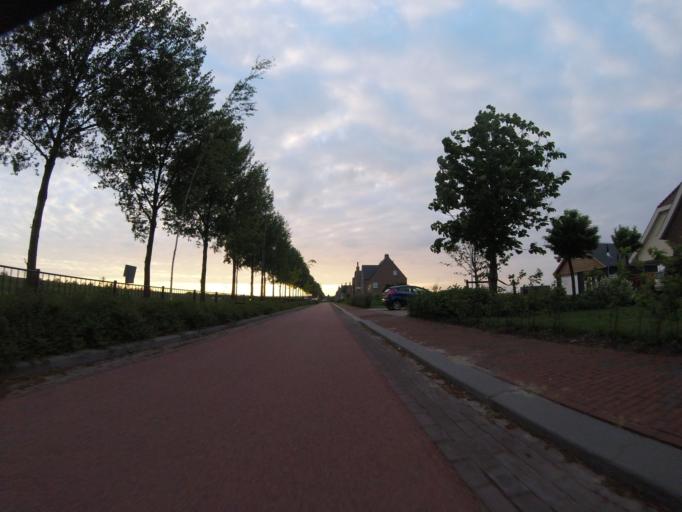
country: NL
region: North Holland
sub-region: Gemeente Haarlemmermeer
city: Hoofddorp
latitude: 52.2892
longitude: 4.6562
